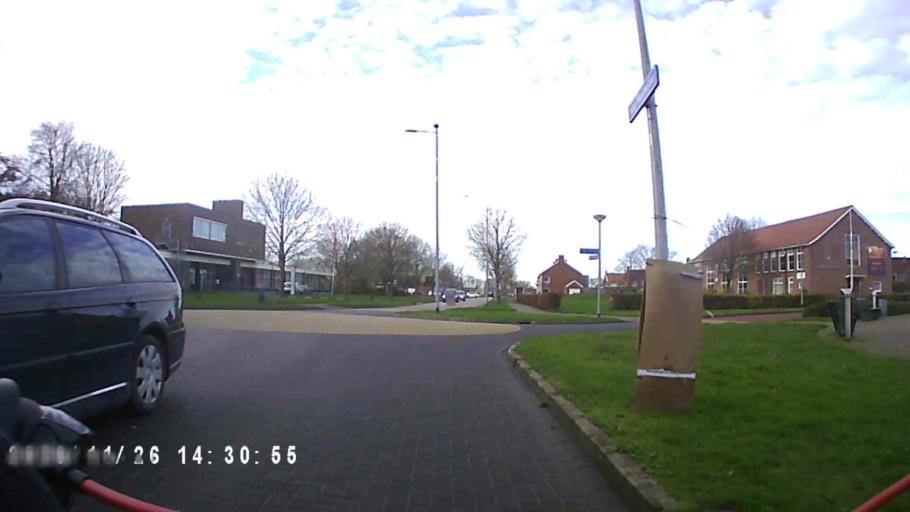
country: NL
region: Groningen
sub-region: Gemeente Appingedam
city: Appingedam
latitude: 53.3157
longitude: 6.8632
